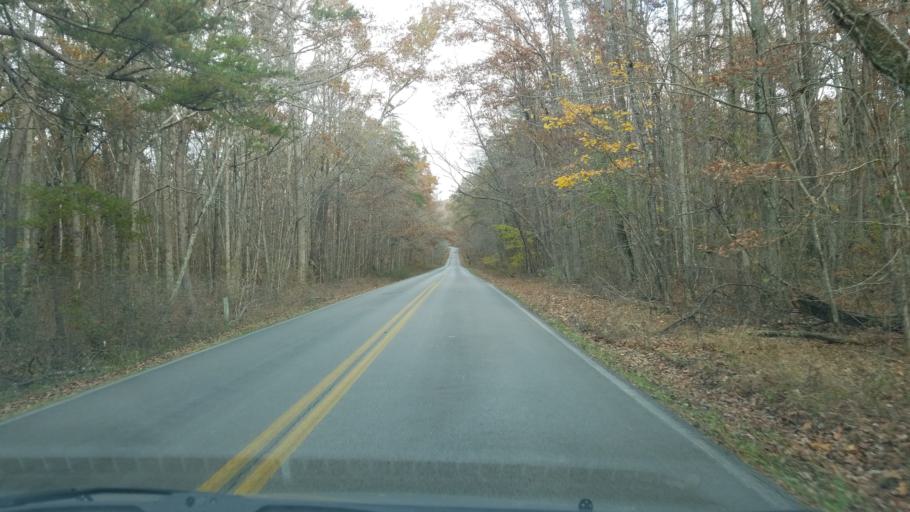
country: US
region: Georgia
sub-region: Dade County
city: Trenton
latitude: 34.8201
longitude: -85.4864
